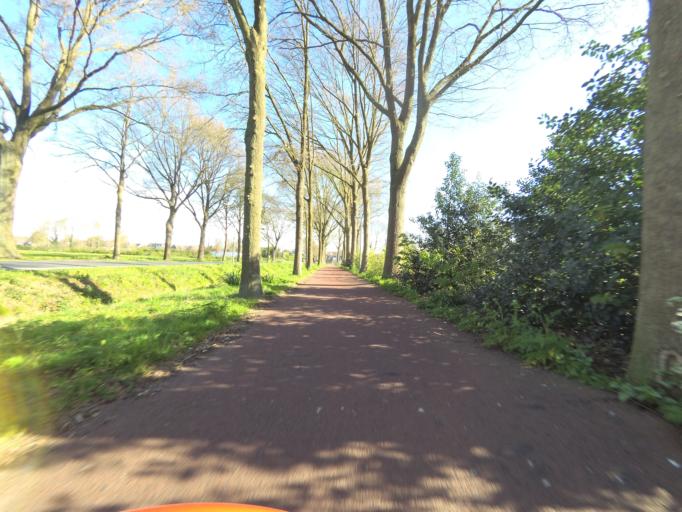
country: NL
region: Gelderland
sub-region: Gemeente Putten
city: Putten
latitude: 52.2520
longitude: 5.5925
